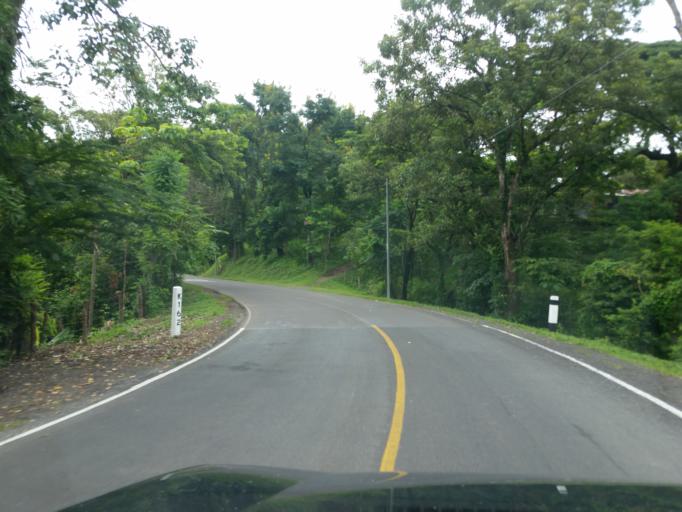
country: NI
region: Matagalpa
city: San Ramon
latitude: 13.0578
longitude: -85.7536
